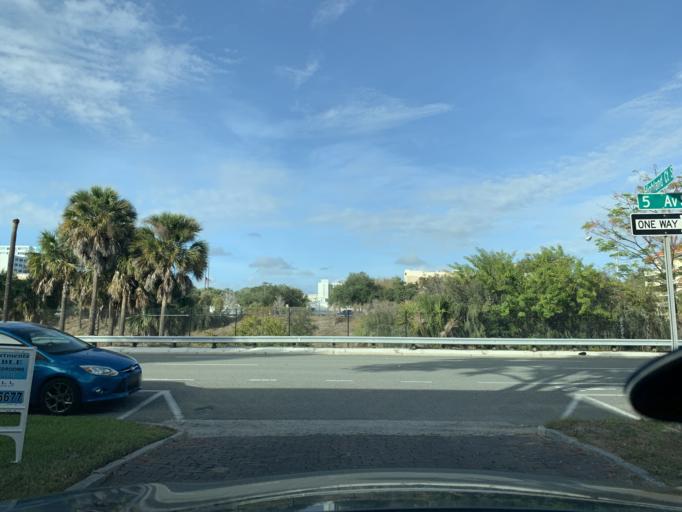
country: US
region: Florida
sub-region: Pinellas County
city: Saint Petersburg
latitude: 27.7655
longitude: -82.6456
